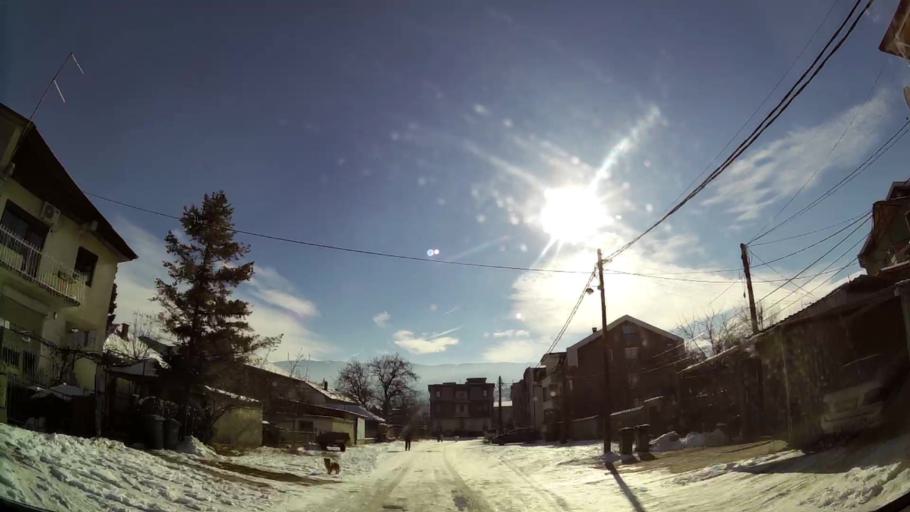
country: MK
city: Krushopek
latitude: 42.0048
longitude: 21.3597
